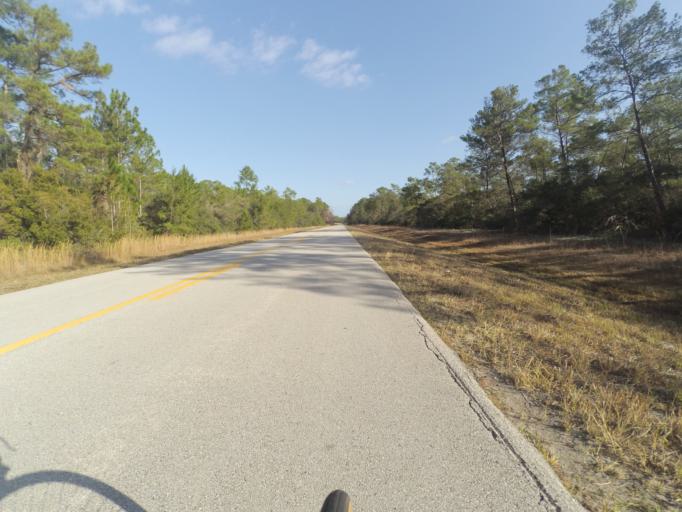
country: US
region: Florida
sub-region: Lake County
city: Astor
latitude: 29.1291
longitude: -81.5782
